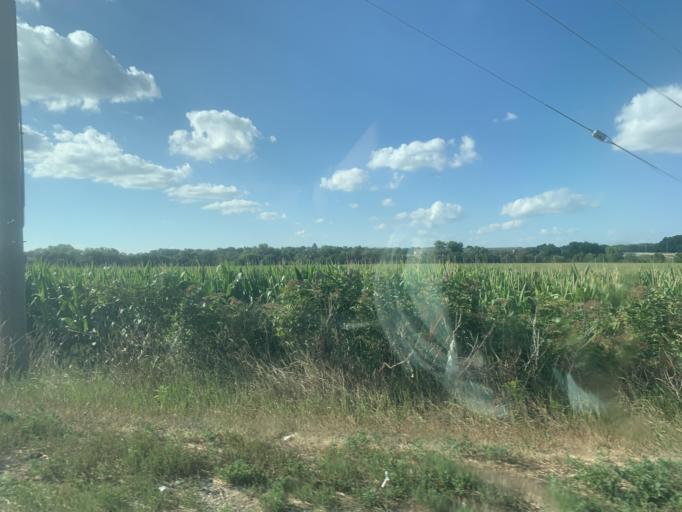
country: US
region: Nebraska
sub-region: Sarpy County
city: Chalco
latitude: 41.1763
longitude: -96.1406
